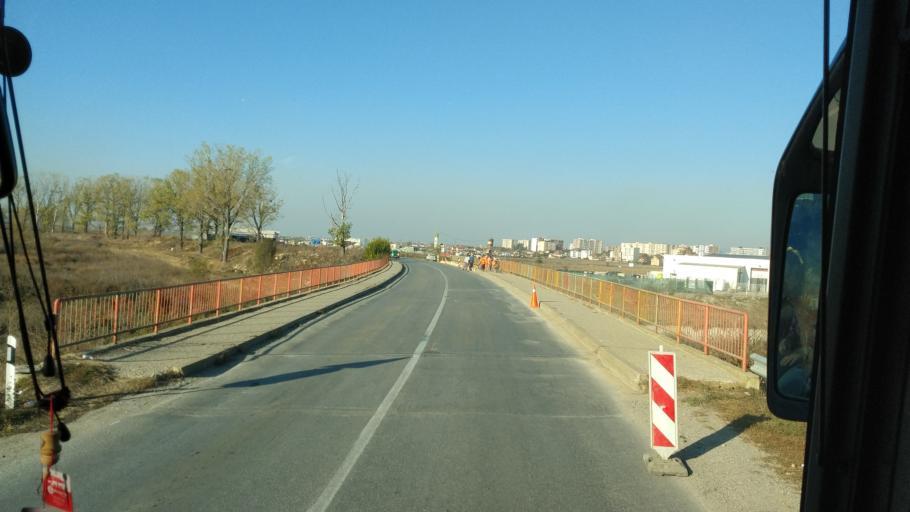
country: XK
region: Pristina
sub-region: Lipjan
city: Lipljan
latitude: 42.5125
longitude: 21.1130
